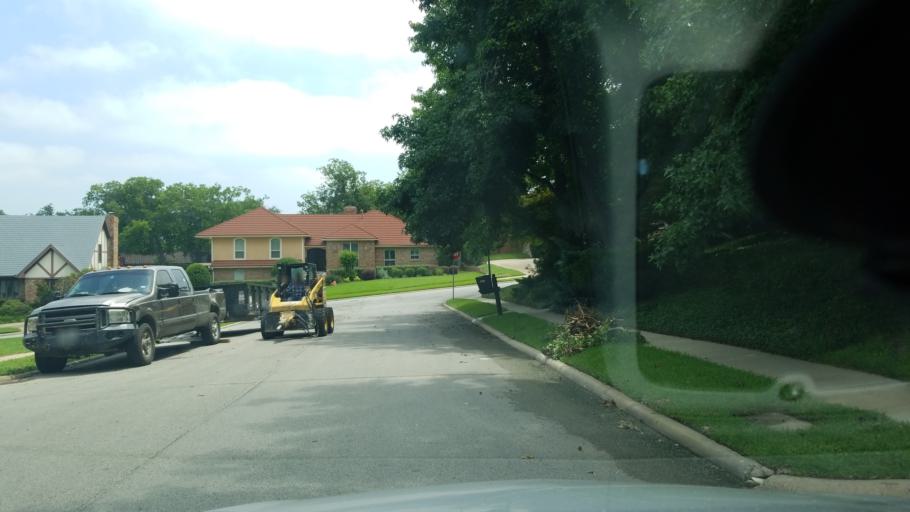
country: US
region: Texas
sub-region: Dallas County
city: Irving
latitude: 32.8564
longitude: -96.9410
